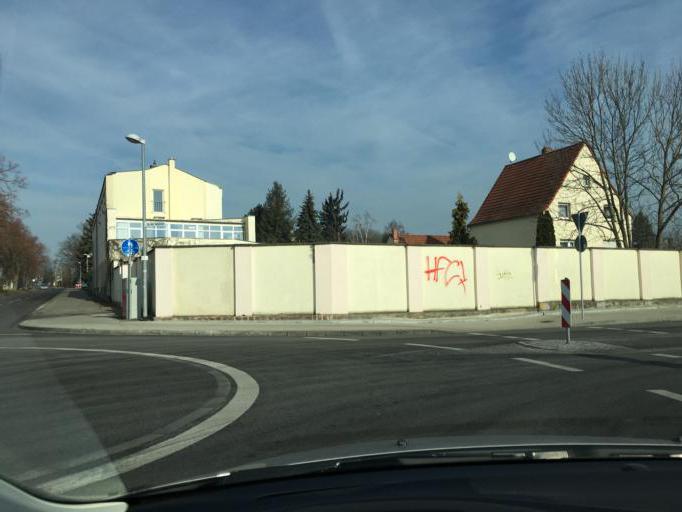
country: DE
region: Saxony-Anhalt
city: Grobers
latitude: 51.4354
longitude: 12.1180
